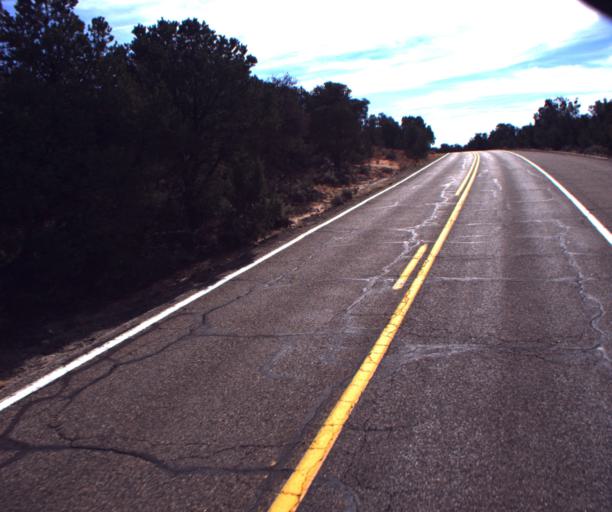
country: US
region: Arizona
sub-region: Navajo County
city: Kayenta
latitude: 36.6486
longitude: -110.5184
